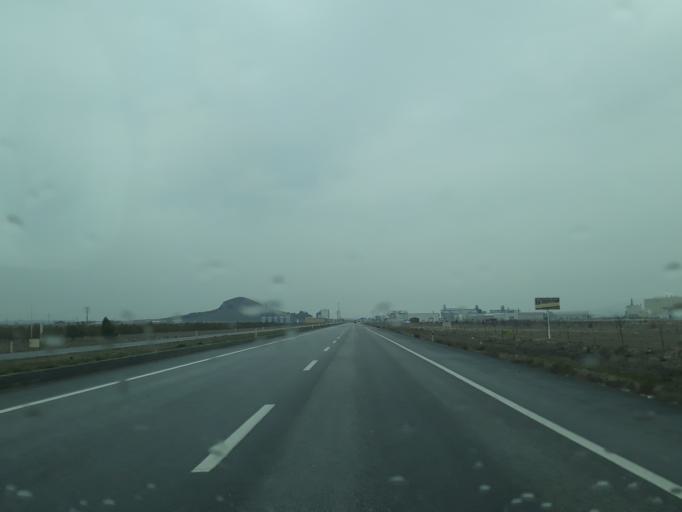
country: TR
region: Konya
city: Karapinar
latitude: 37.7128
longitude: 33.6025
